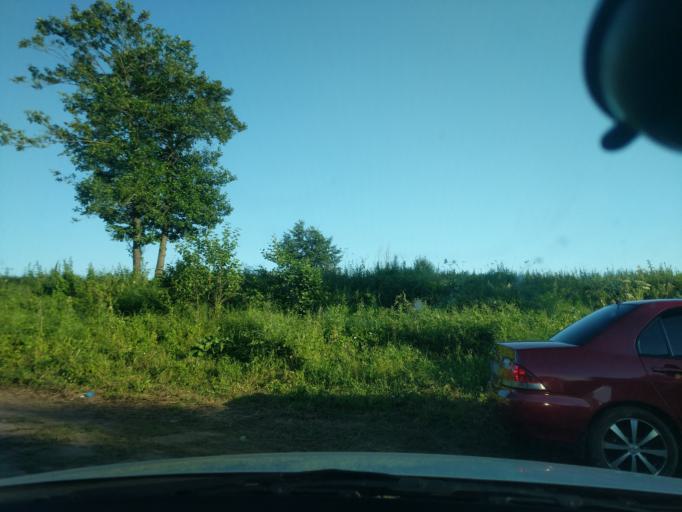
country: RU
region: Moskovskaya
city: Pushchino
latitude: 54.8493
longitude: 37.6456
